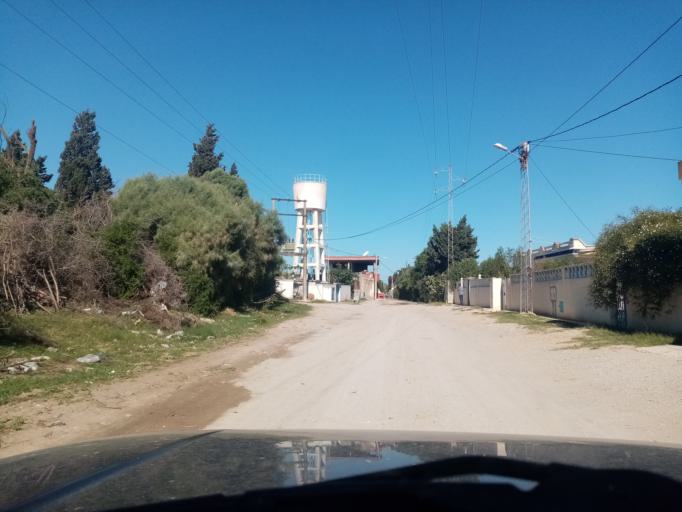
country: TN
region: Nabul
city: Bu `Urqub
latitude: 36.5741
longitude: 10.5733
